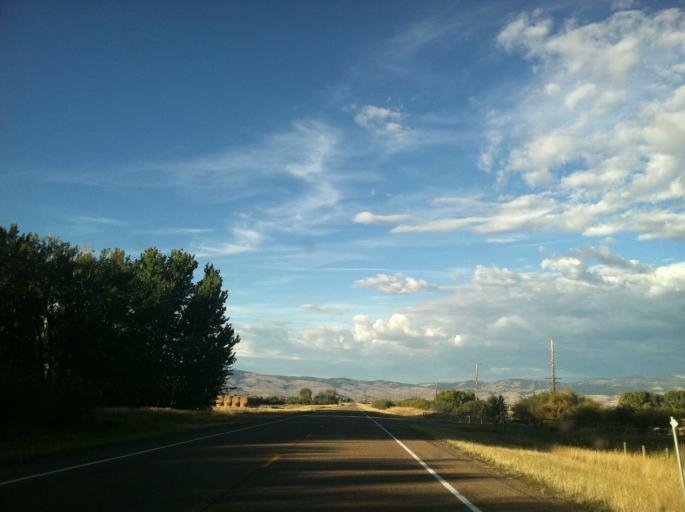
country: US
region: Montana
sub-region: Granite County
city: Philipsburg
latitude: 46.5635
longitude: -113.2113
